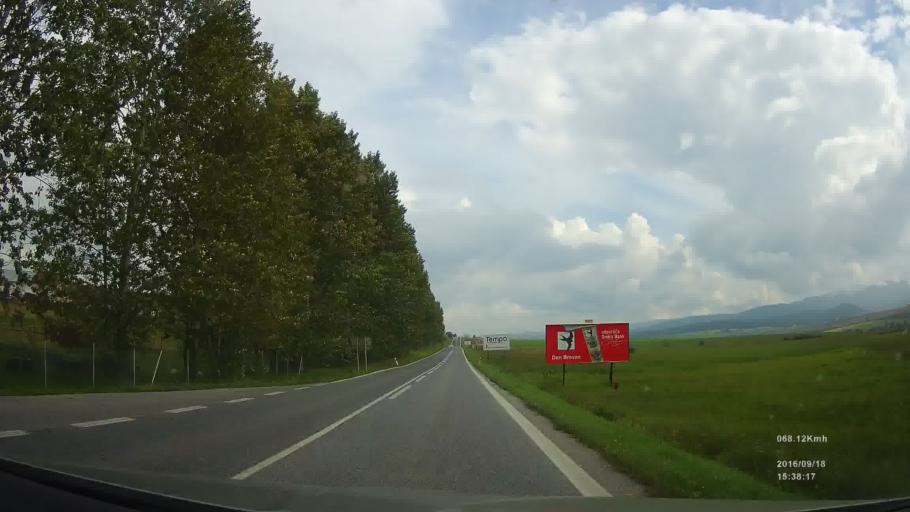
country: SK
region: Kosicky
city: Spisska Nova Ves
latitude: 48.9744
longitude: 20.4908
